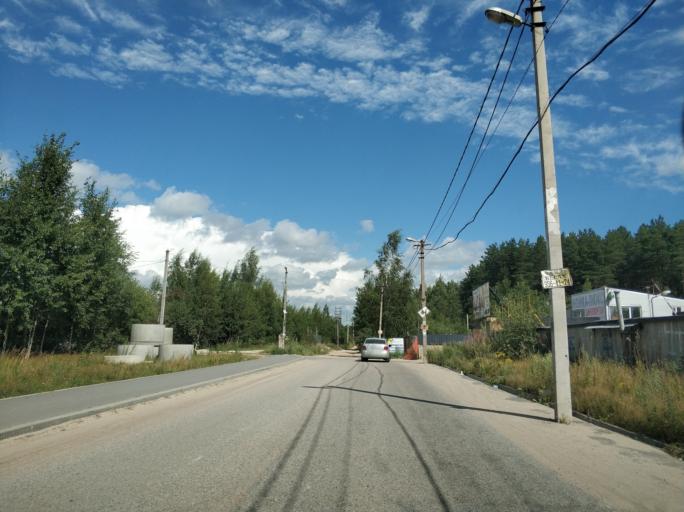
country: RU
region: Leningrad
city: Vsevolozhsk
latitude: 60.0227
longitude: 30.6094
